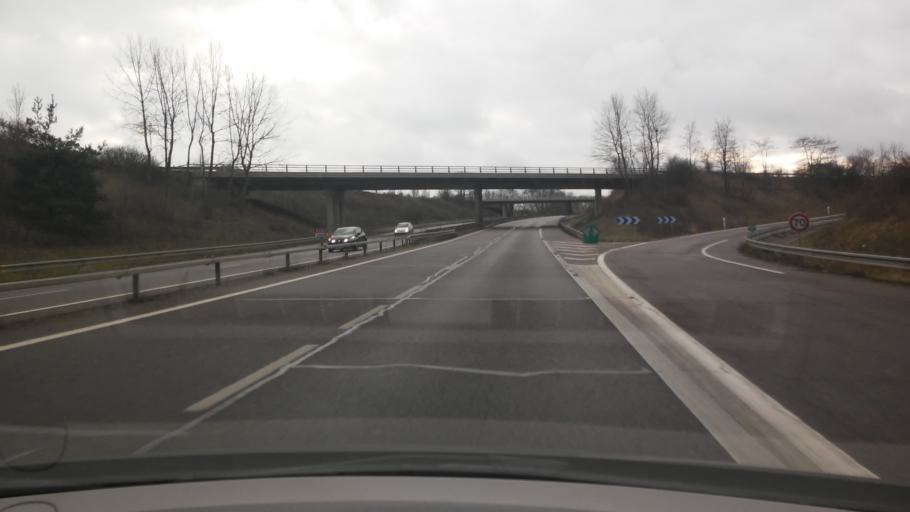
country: FR
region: Lorraine
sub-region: Departement de la Moselle
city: Saint-Julien-les-Metz
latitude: 49.1280
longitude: 6.2413
